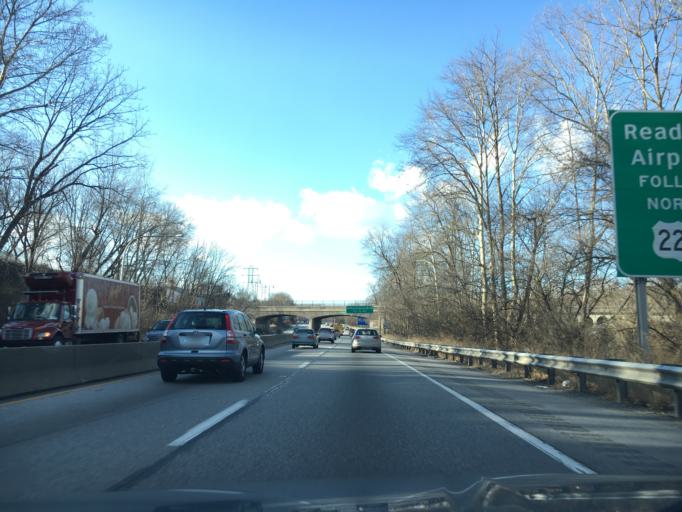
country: US
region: Pennsylvania
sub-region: Berks County
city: West Reading
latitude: 40.3380
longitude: -75.9421
